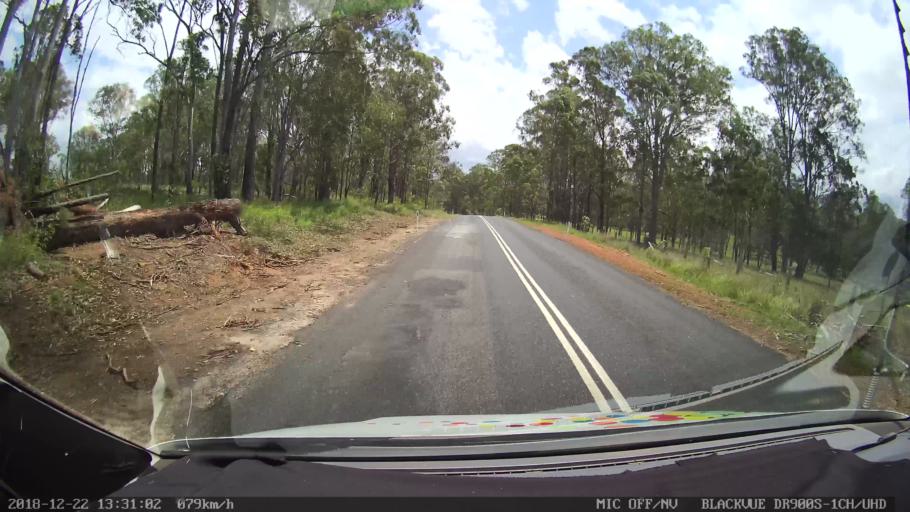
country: AU
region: New South Wales
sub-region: Clarence Valley
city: Coutts Crossing
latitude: -29.8532
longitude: 152.8576
